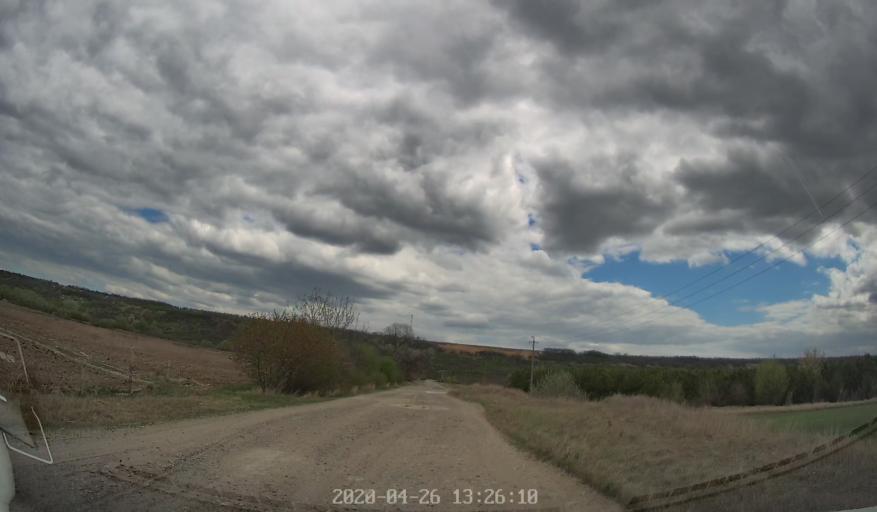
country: MD
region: Criuleni
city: Criuleni
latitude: 47.2059
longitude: 29.1713
